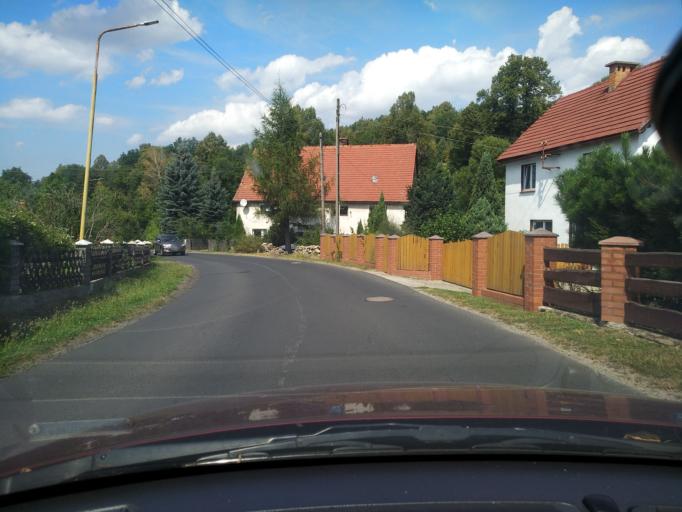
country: PL
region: Lower Silesian Voivodeship
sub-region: Powiat jeleniogorski
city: Stara Kamienica
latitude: 50.9005
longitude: 15.5727
